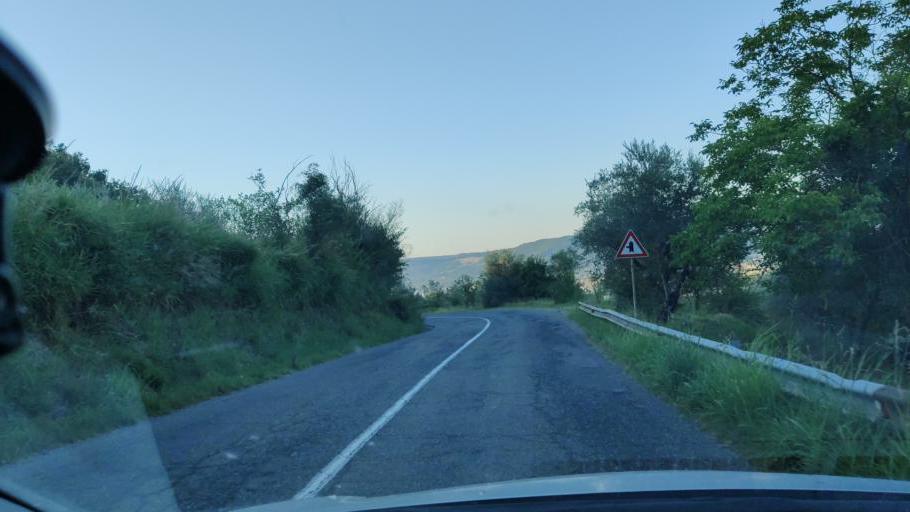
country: IT
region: Umbria
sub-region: Provincia di Terni
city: Giove
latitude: 42.5029
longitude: 12.3216
